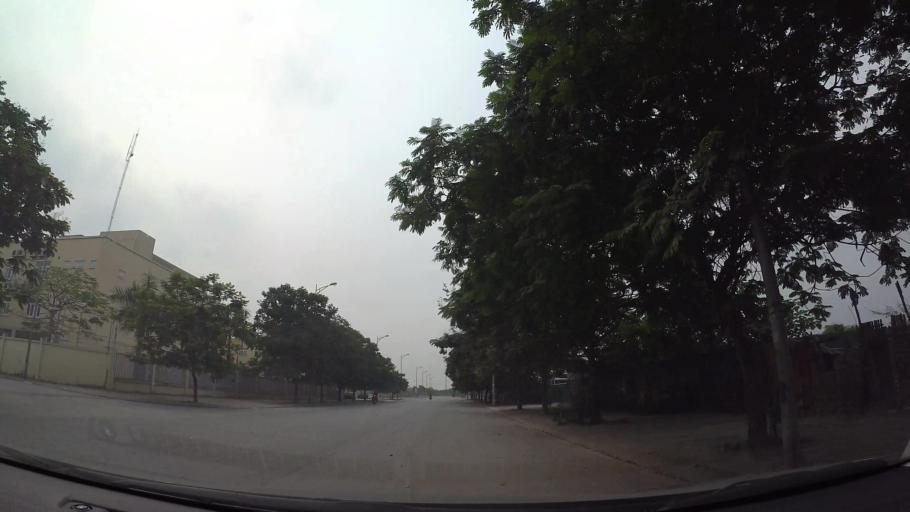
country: VN
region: Ha Noi
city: Trau Quy
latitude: 21.0721
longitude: 105.8996
